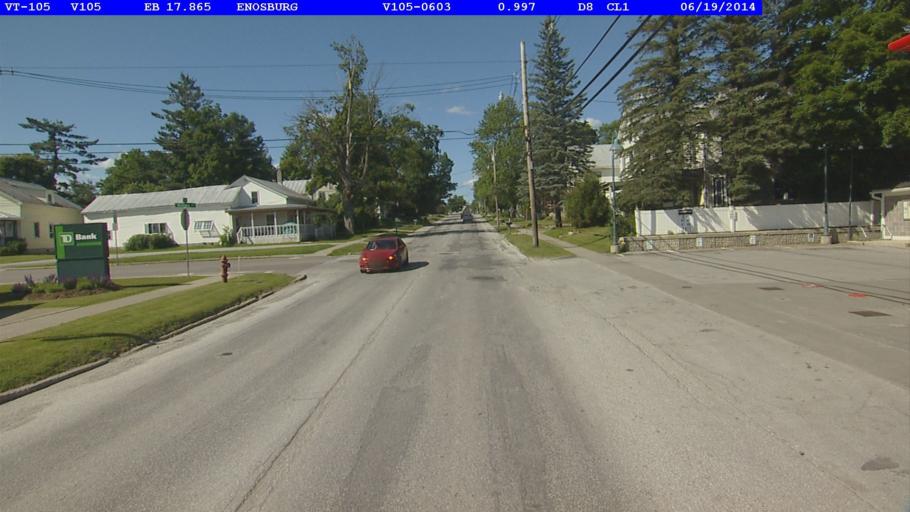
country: US
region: Vermont
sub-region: Franklin County
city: Enosburg Falls
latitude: 44.9085
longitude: -72.8044
